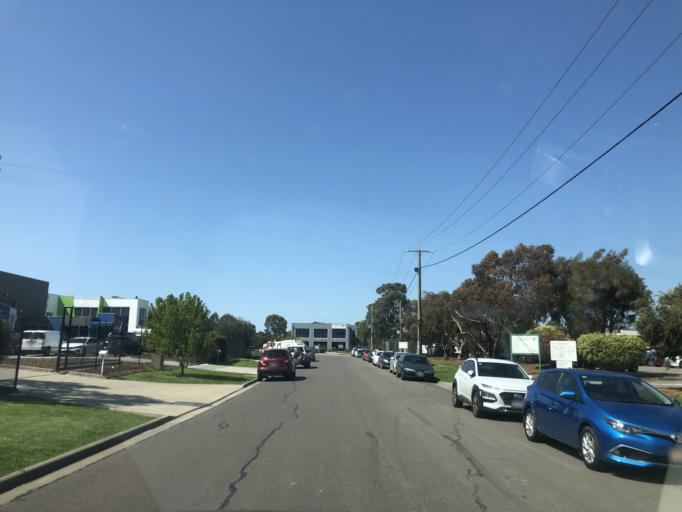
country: AU
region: Victoria
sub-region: Casey
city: Hampton Park
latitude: -38.0198
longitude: 145.2445
